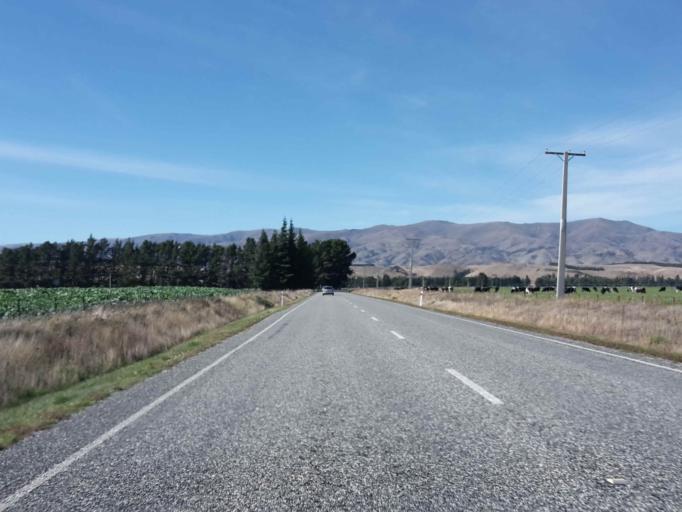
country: NZ
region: Otago
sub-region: Queenstown-Lakes District
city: Wanaka
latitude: -44.8251
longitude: 169.3589
